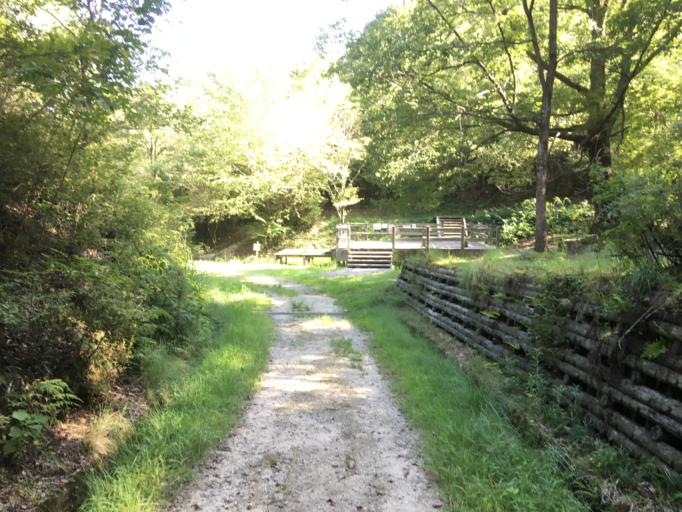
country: JP
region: Osaka
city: Neyagawa
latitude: 34.7488
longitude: 135.6844
